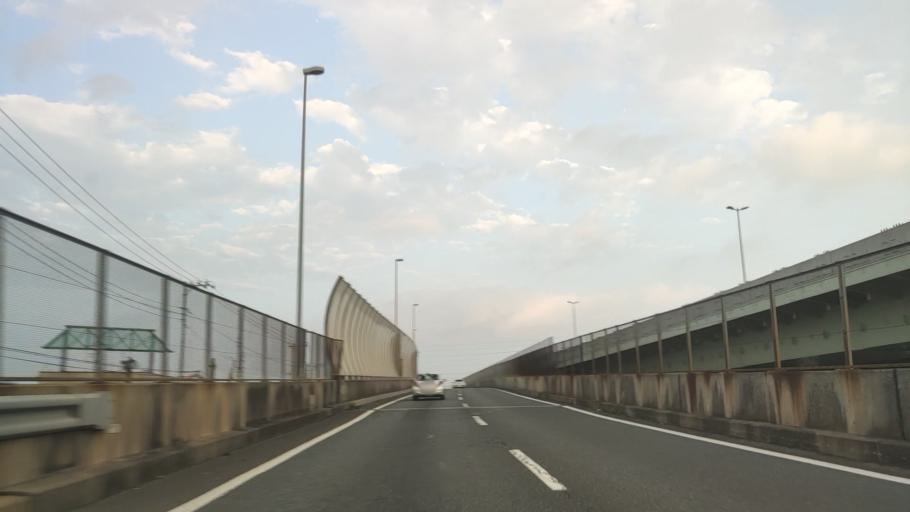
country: JP
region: Kanagawa
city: Minami-rinkan
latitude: 35.5051
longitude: 139.4838
